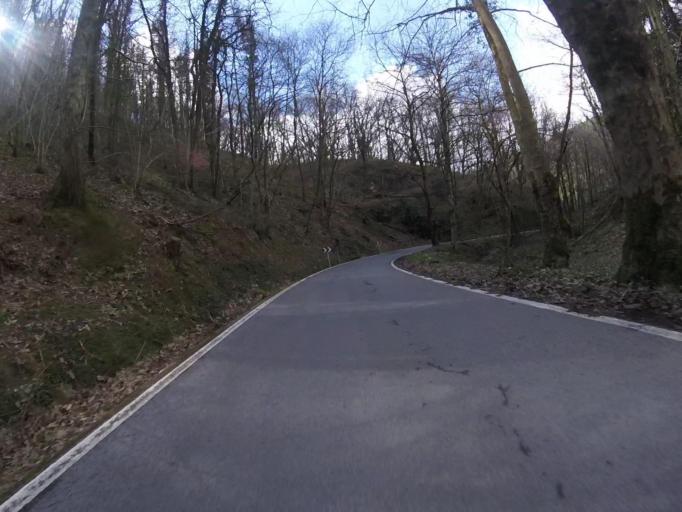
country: ES
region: Navarre
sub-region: Provincia de Navarra
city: Etxalar
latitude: 43.2399
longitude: -1.6316
